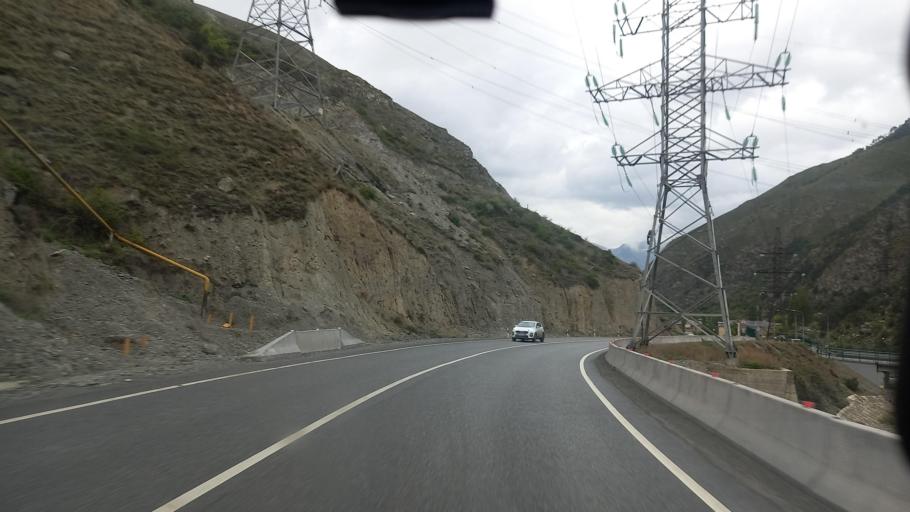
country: RU
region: North Ossetia
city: Mizur
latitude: 42.8460
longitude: 44.0422
